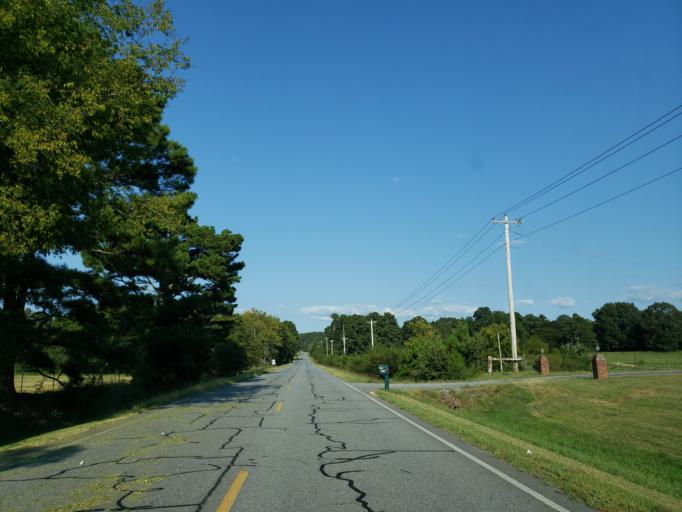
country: US
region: Georgia
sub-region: Whitfield County
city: Varnell
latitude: 34.9312
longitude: -84.8122
